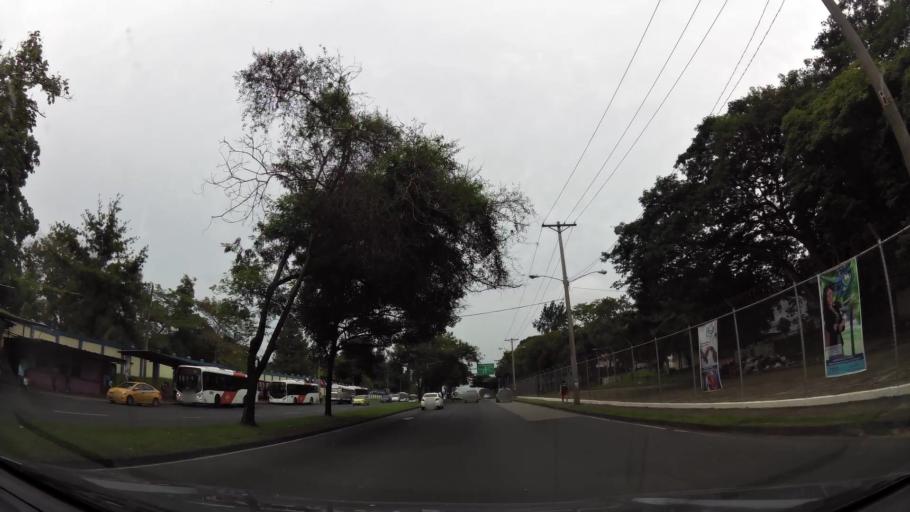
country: PA
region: Panama
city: Panama
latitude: 8.9847
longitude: -79.5351
